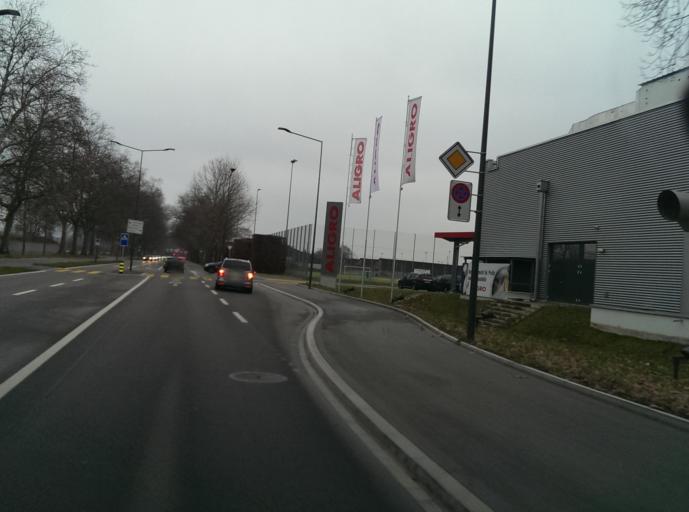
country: CH
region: Zurich
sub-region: Bezirk Dietikon
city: Oberengstringen / Zentrum
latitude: 47.3998
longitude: 8.4672
